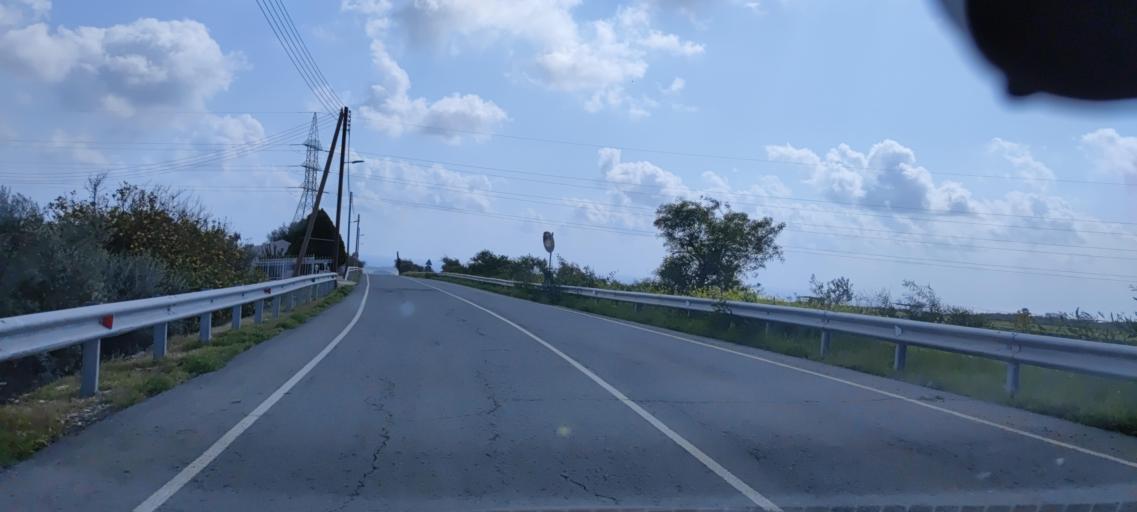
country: CY
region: Pafos
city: Paphos
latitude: 34.7436
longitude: 32.4983
